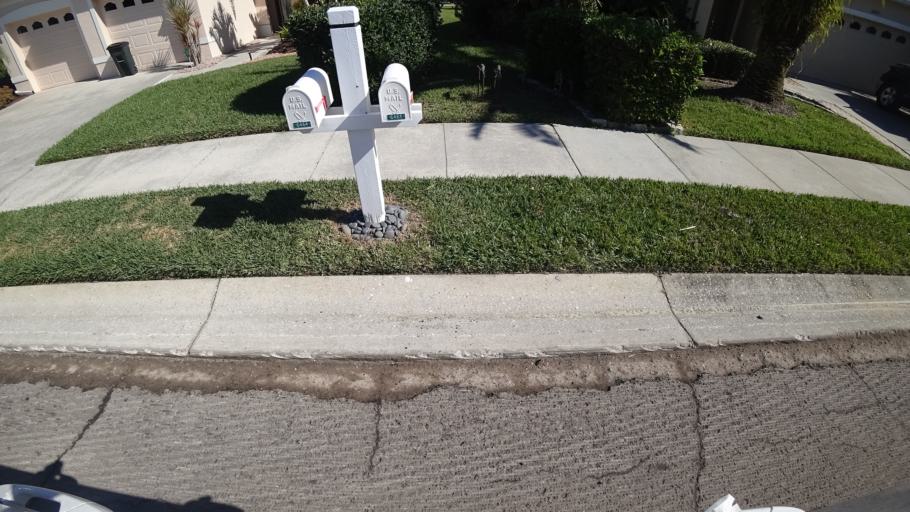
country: US
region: Florida
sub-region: Sarasota County
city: Desoto Lakes
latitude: 27.4272
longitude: -82.4651
